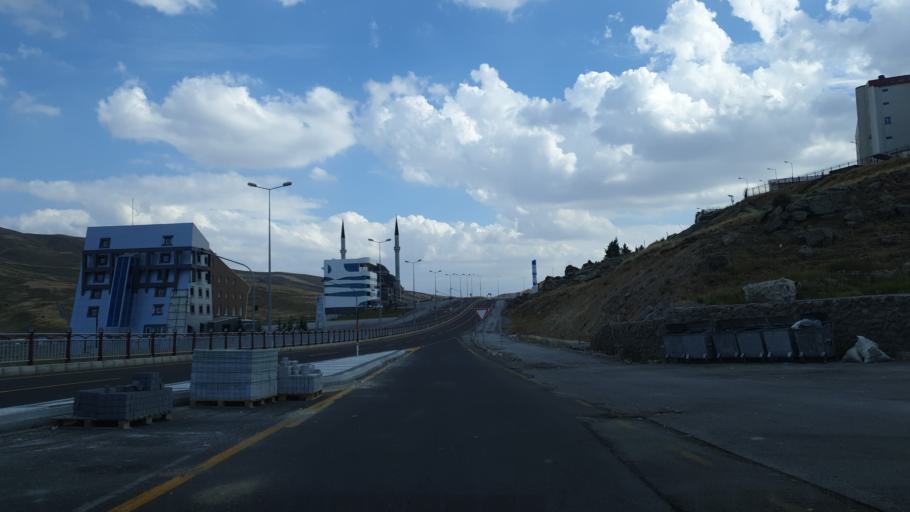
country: TR
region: Kayseri
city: Hacilar
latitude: 38.5436
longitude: 35.5266
